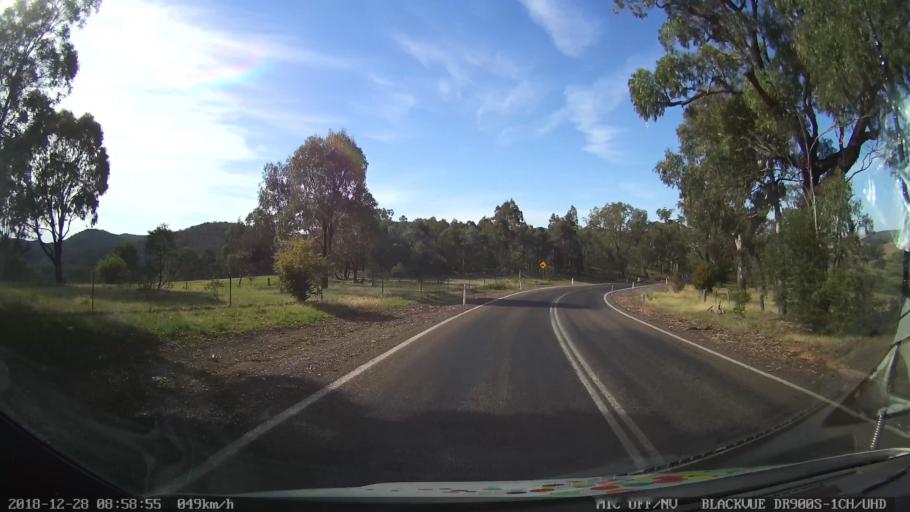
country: AU
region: New South Wales
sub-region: Upper Lachlan Shire
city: Crookwell
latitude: -34.1305
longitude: 149.3329
